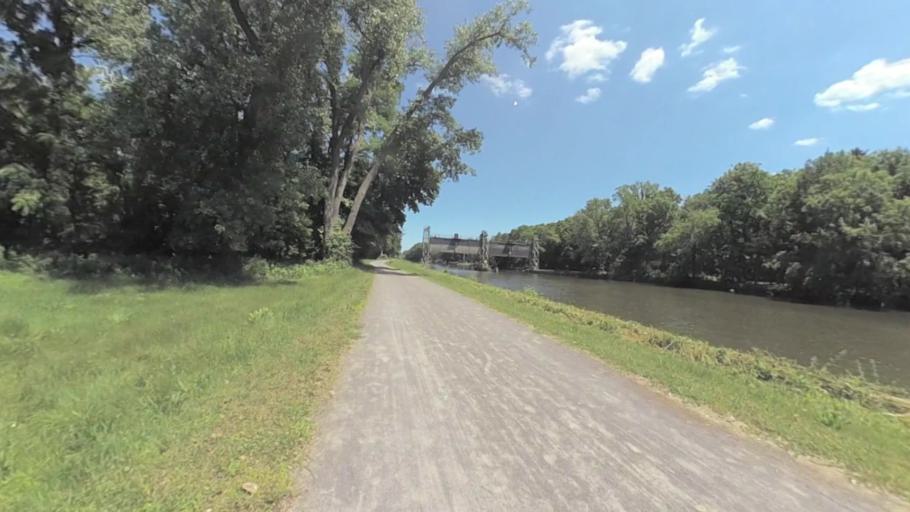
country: US
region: New York
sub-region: Monroe County
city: Fairport
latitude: 43.0679
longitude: -77.4693
